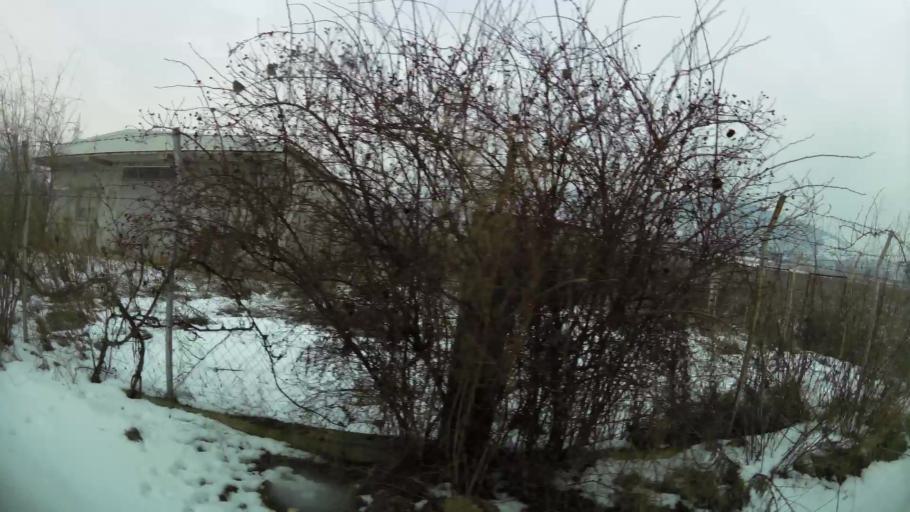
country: MK
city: Kondovo
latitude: 42.0392
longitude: 21.3397
